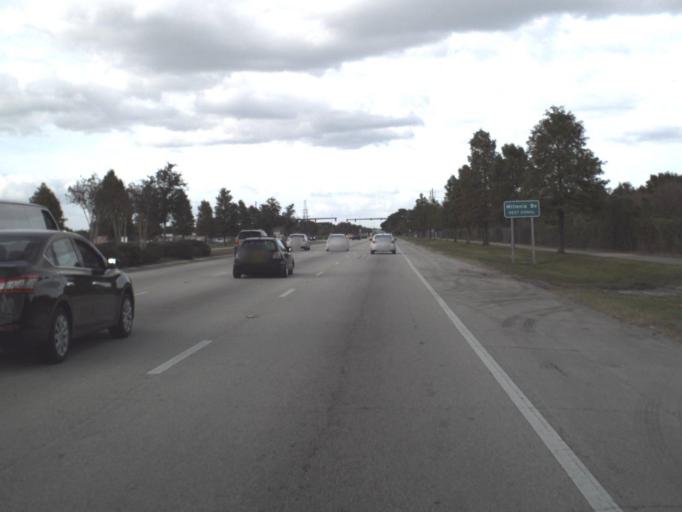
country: US
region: Florida
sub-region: Orange County
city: Oak Ridge
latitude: 28.4914
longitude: -81.4173
